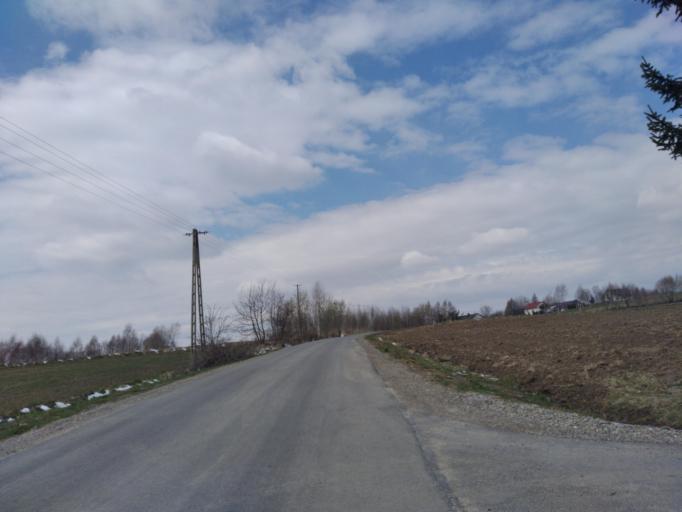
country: PL
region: Subcarpathian Voivodeship
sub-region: Powiat ropczycko-sedziszowski
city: Ropczyce
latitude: 50.0127
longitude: 21.5785
